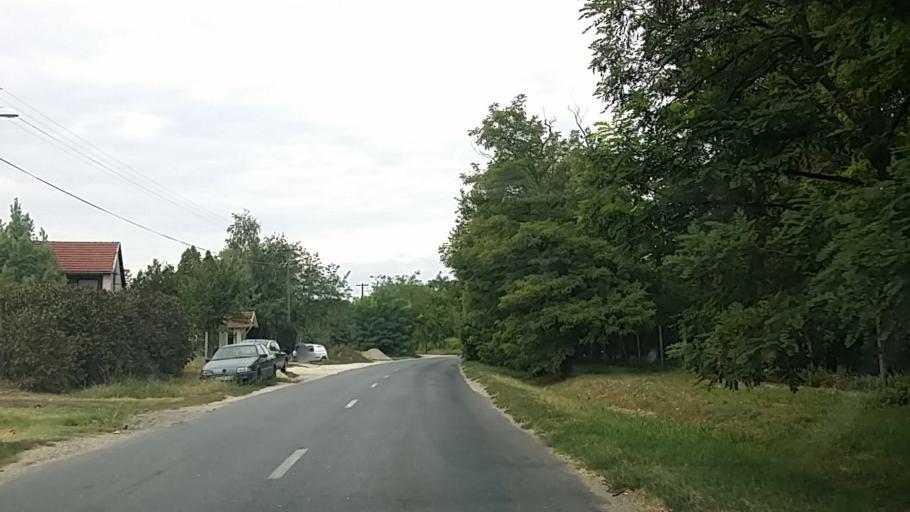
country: HU
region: Komarom-Esztergom
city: Komarom
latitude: 47.7248
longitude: 18.1612
